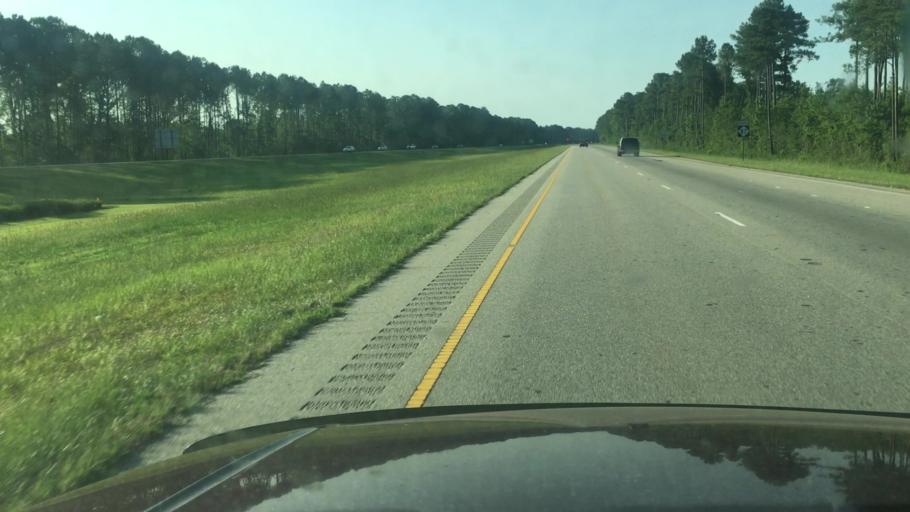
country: US
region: North Carolina
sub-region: Cumberland County
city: Vander
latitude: 34.9703
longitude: -78.8523
